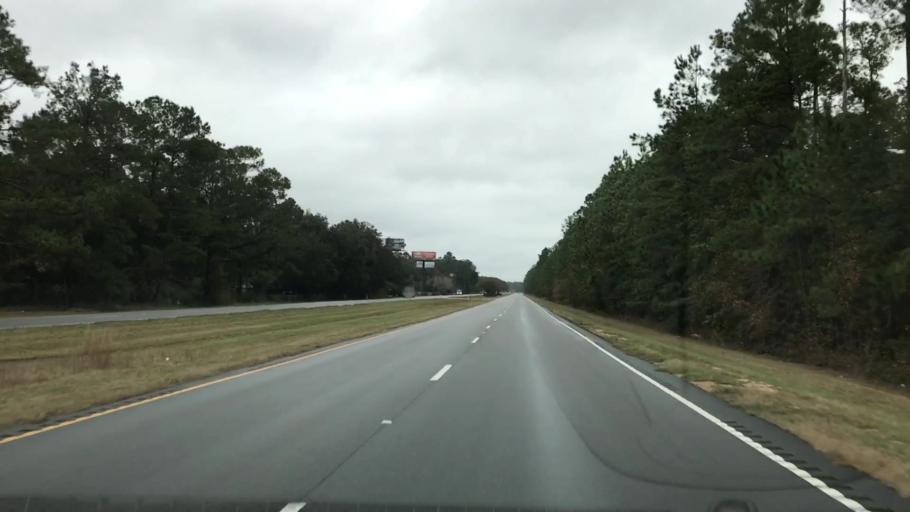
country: US
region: South Carolina
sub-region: Georgetown County
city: Georgetown
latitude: 33.2328
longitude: -79.3760
